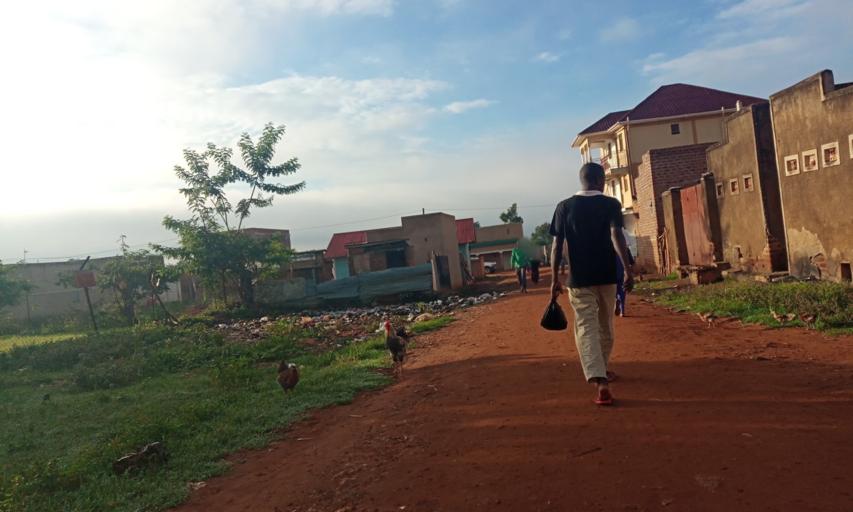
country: UG
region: Eastern Region
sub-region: Mbale District
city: Mbale
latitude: 1.1413
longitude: 34.1651
